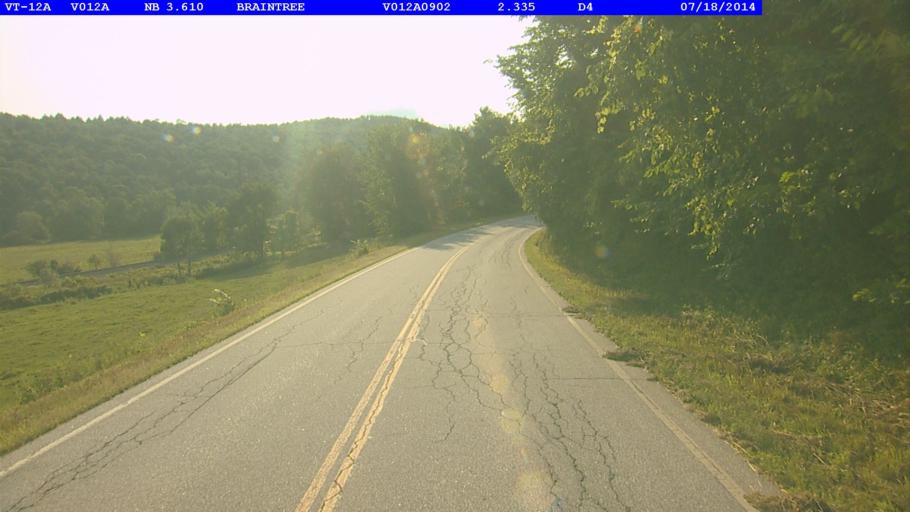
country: US
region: Vermont
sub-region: Orange County
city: Randolph
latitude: 43.9509
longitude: -72.7188
